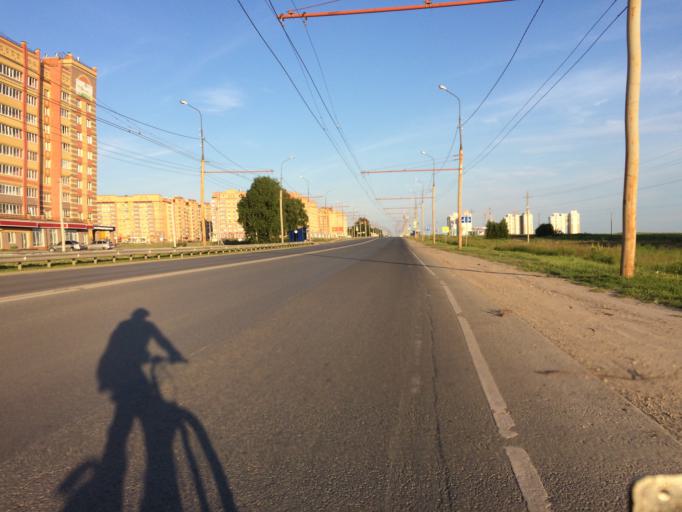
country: RU
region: Mariy-El
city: Medvedevo
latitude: 56.6399
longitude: 47.8212
